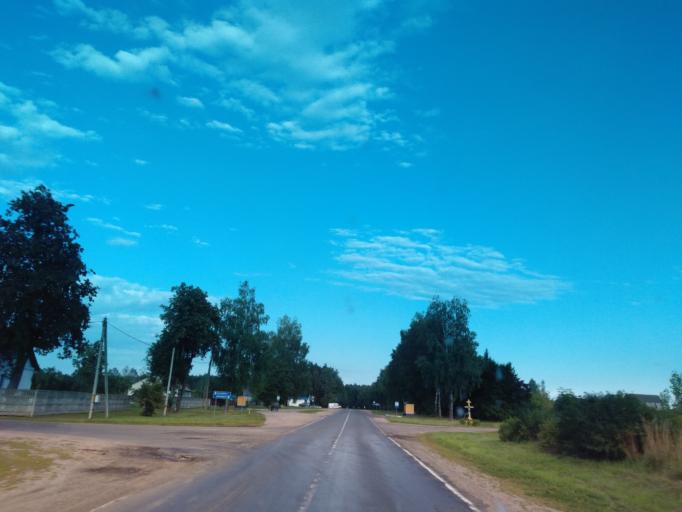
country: BY
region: Minsk
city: Uzda
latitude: 53.4194
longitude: 27.4079
